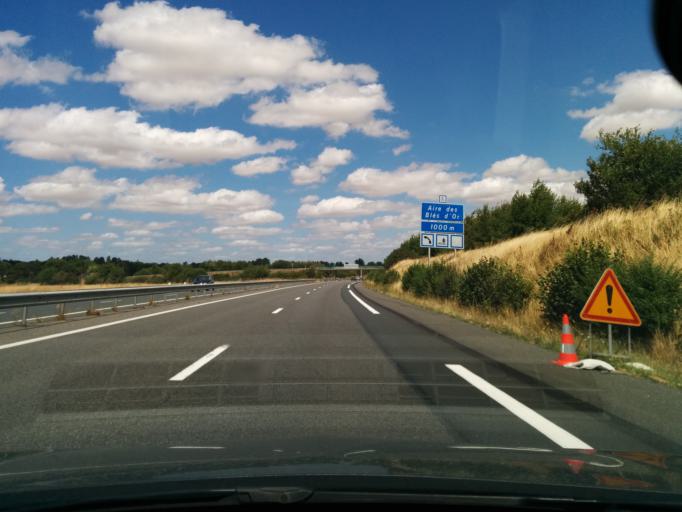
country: FR
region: Centre
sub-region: Departement de l'Indre
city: Deols
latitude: 46.8739
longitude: 1.7157
